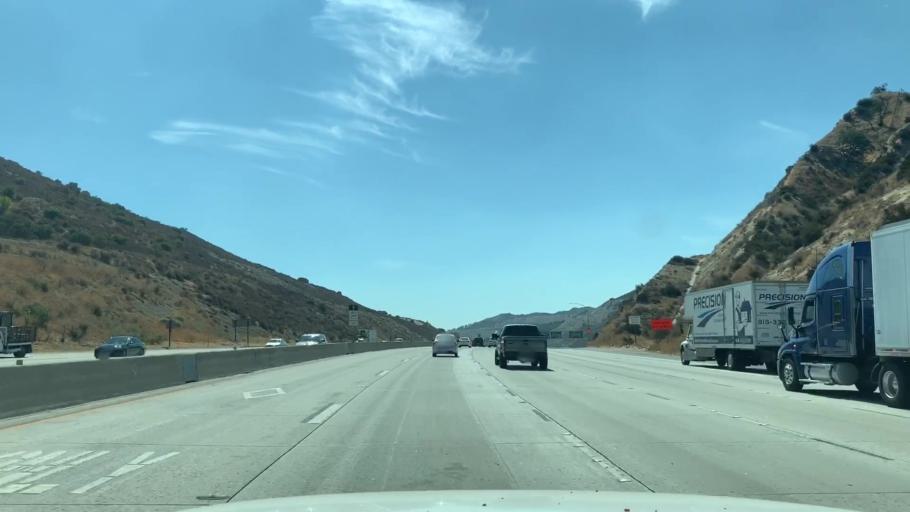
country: US
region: California
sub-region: Los Angeles County
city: Santa Clarita
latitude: 34.3466
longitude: -118.5041
